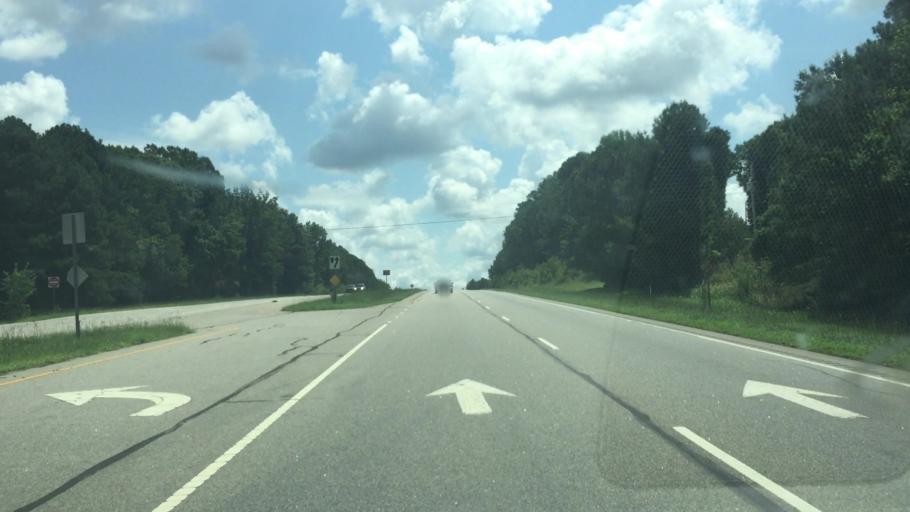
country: US
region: North Carolina
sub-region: Anson County
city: Wadesboro
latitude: 34.9634
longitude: -80.0160
